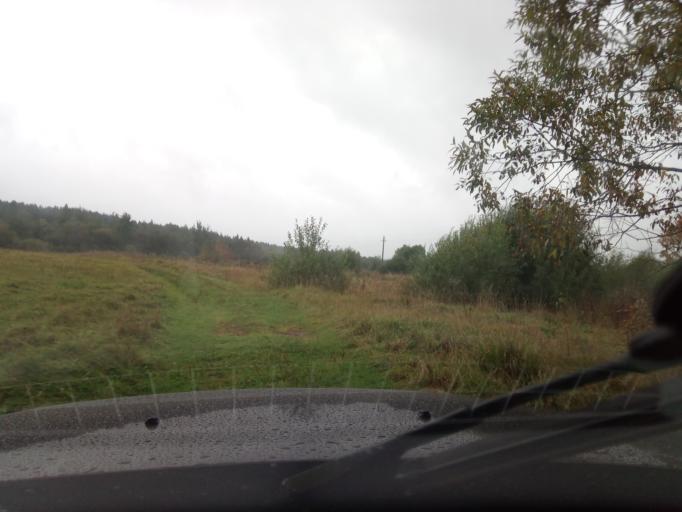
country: LT
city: Skaidiskes
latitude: 54.5977
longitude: 25.5852
